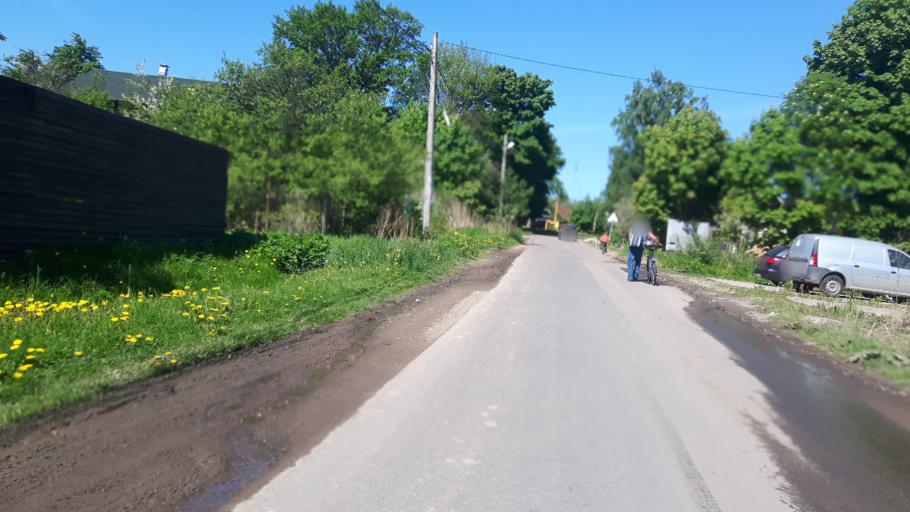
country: RU
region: Leningrad
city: Lebyazh'ye
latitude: 59.9681
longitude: 29.3949
